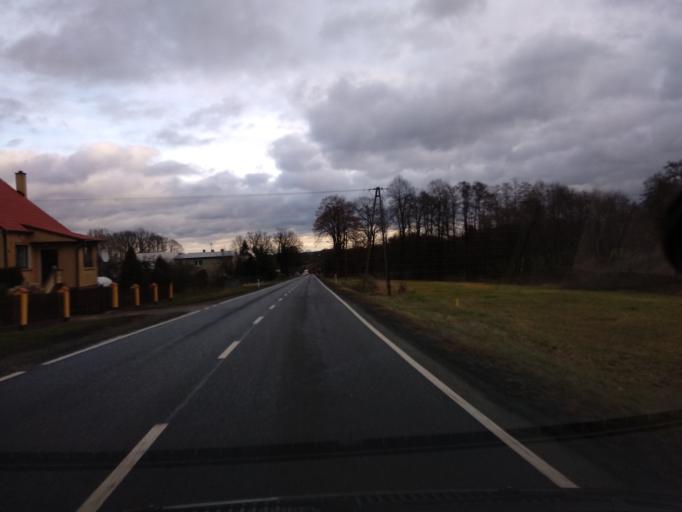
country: PL
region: Lower Silesian Voivodeship
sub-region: Powiat olesnicki
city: Miedzyborz
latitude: 51.3823
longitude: 17.6377
